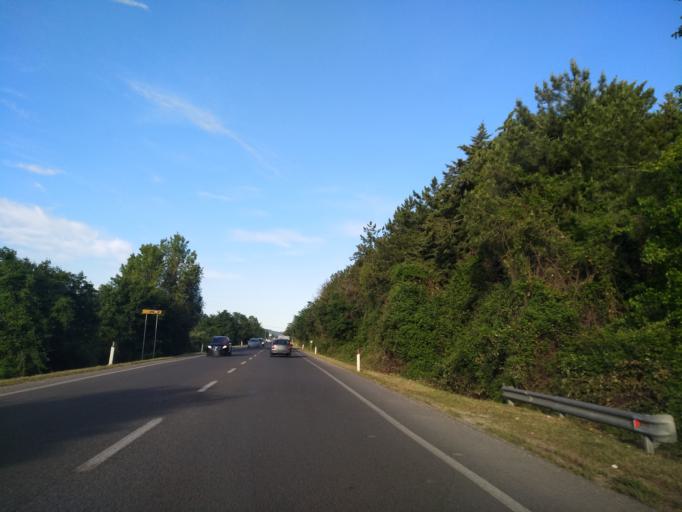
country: IT
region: The Marches
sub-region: Provincia di Pesaro e Urbino
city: Villa Ceccolini
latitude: 43.8825
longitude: 12.8566
